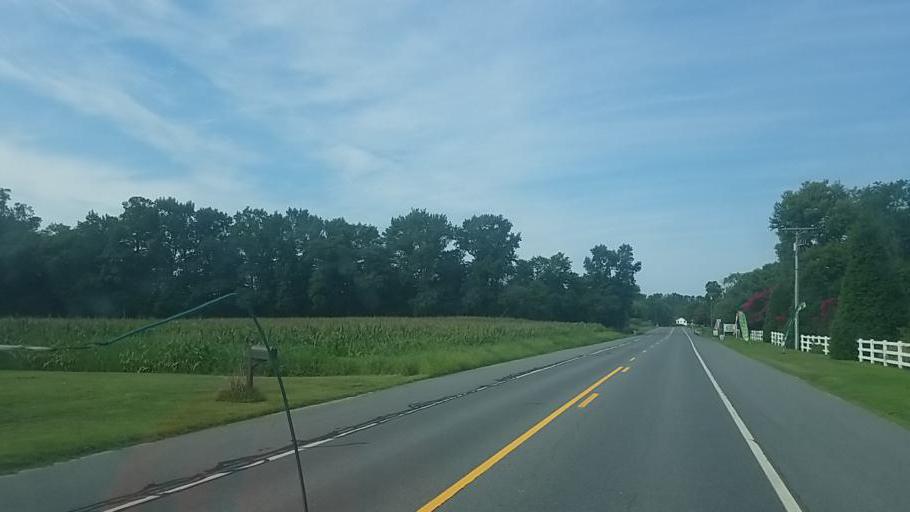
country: US
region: Delaware
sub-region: Sussex County
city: Selbyville
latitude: 38.5294
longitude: -75.1951
